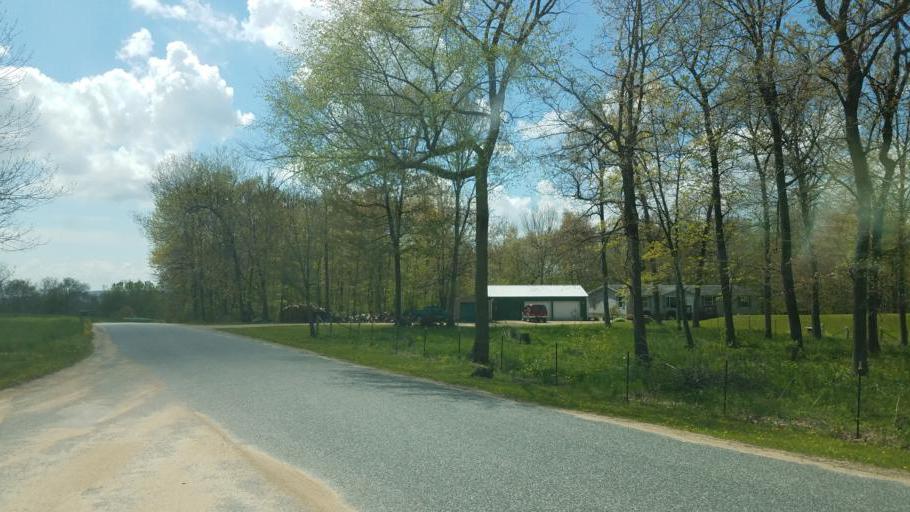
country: US
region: Wisconsin
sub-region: Vernon County
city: Hillsboro
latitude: 43.6913
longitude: -90.3189
